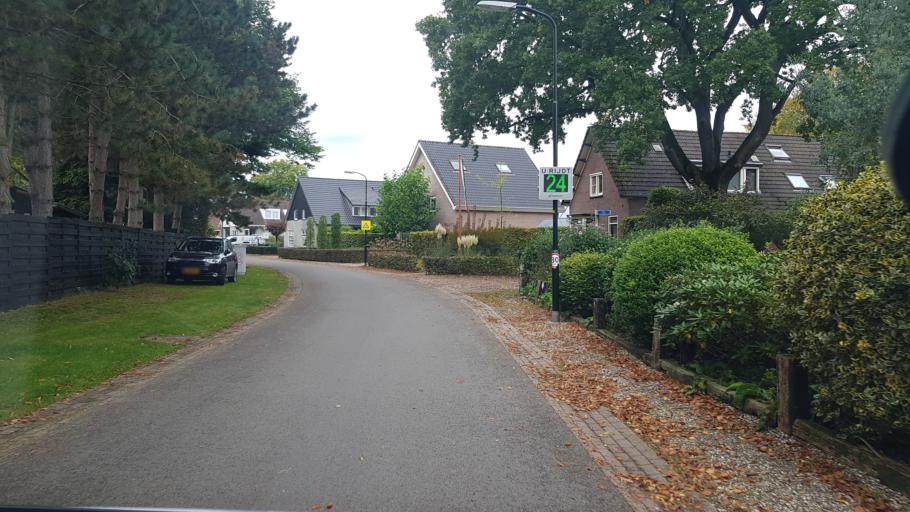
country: NL
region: Gelderland
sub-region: Gemeente Apeldoorn
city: Loenen
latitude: 52.1157
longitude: 6.0227
